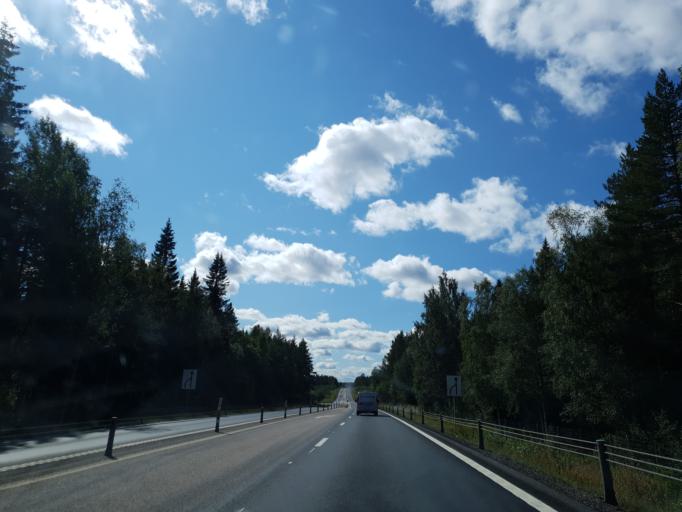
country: SE
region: Vaesterbotten
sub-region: Nordmalings Kommun
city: Nordmaling
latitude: 63.5138
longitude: 19.3615
